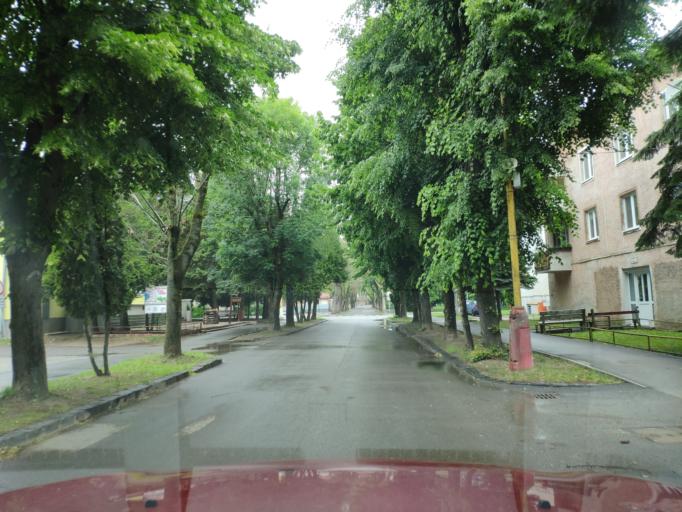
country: SK
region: Kosicky
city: Cierna nad Tisou
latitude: 48.4171
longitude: 22.0890
